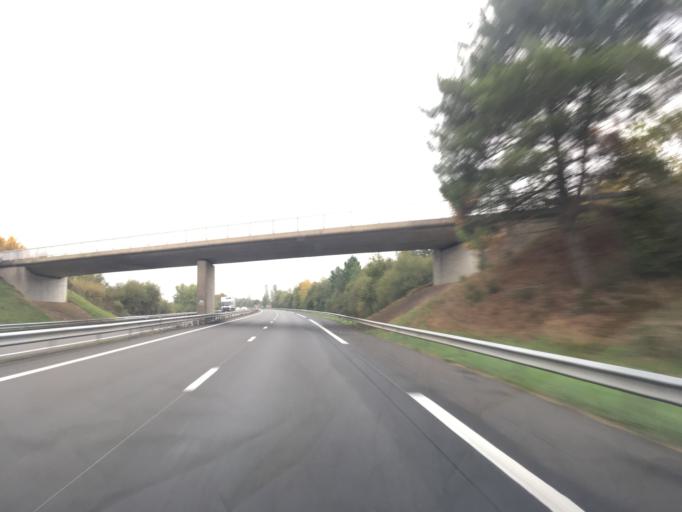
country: FR
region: Pays de la Loire
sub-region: Departement de Maine-et-Loire
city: Durtal
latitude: 47.6298
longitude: -0.2765
